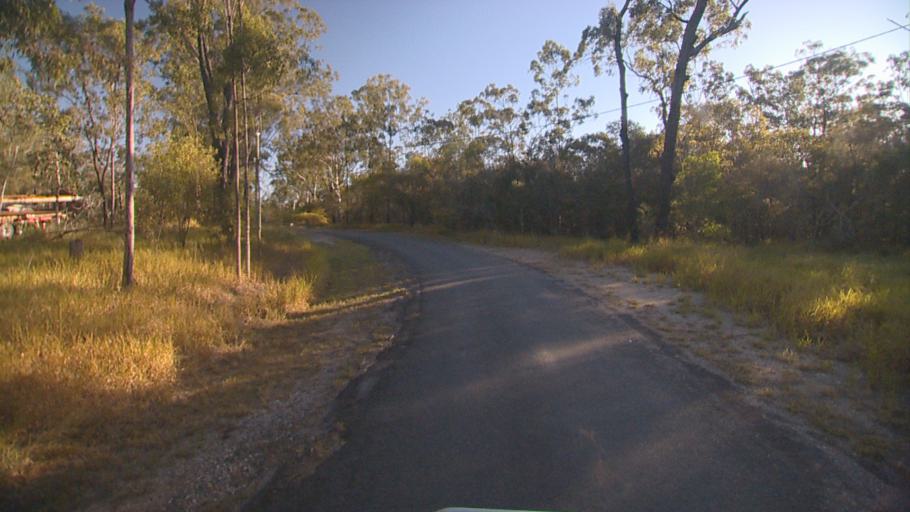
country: AU
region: Queensland
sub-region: Logan
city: Chambers Flat
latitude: -27.8050
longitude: 153.0631
